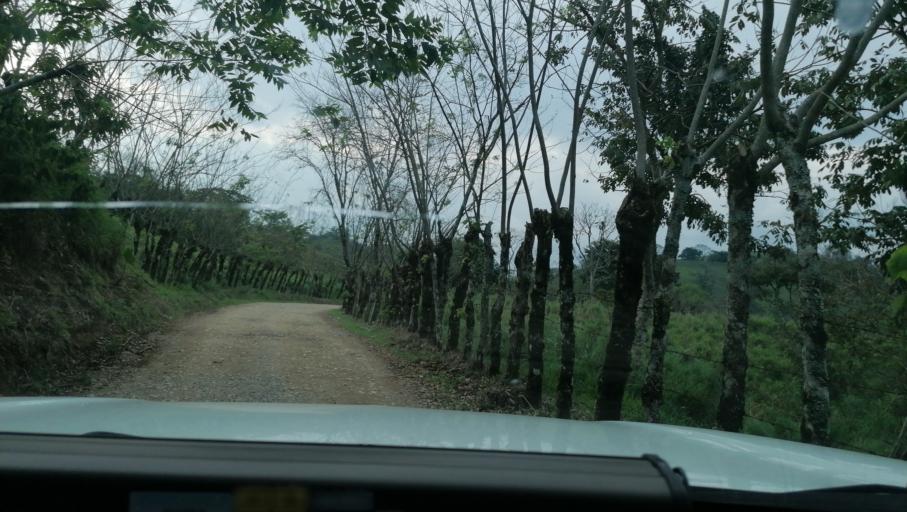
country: MX
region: Chiapas
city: Ixtacomitan
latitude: 17.3389
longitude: -93.1145
